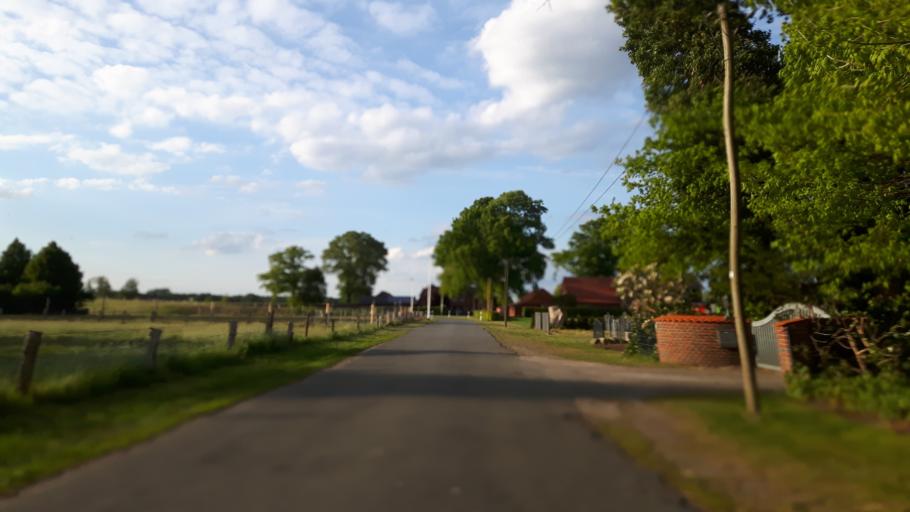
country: DE
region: Lower Saxony
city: Delmenhorst
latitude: 53.0233
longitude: 8.6013
